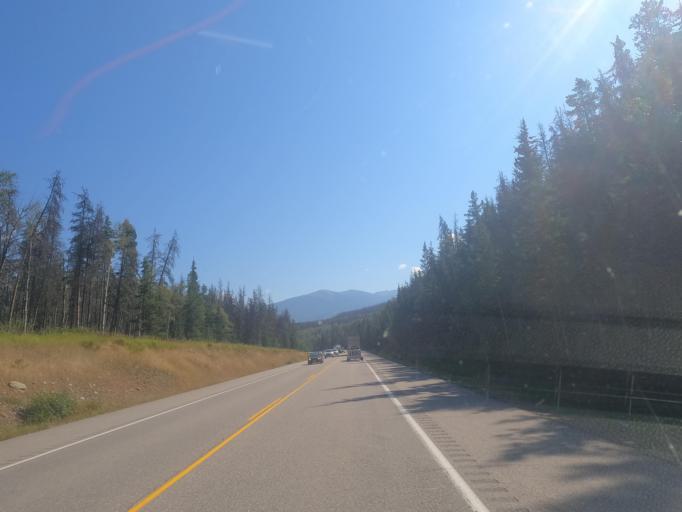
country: CA
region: Alberta
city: Jasper Park Lodge
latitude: 52.8575
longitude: -118.1235
